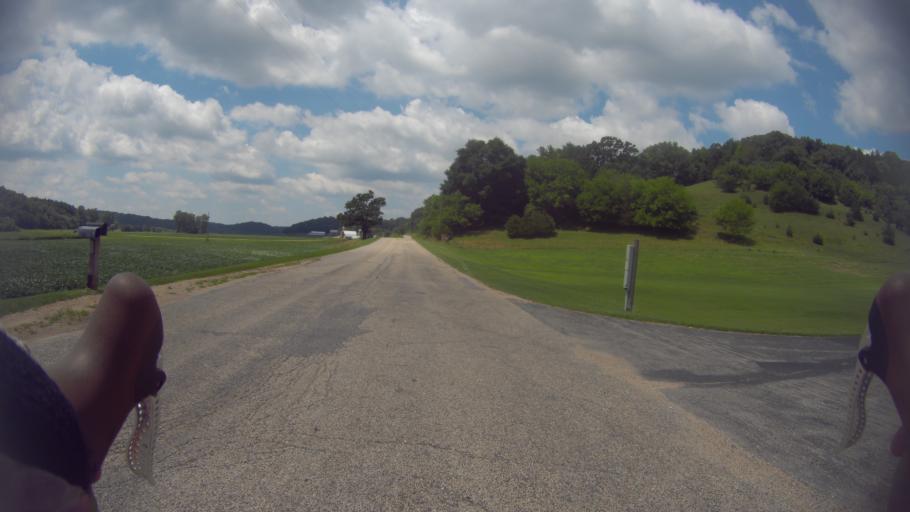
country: US
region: Wisconsin
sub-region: Dane County
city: Black Earth
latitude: 43.1648
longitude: -89.7083
